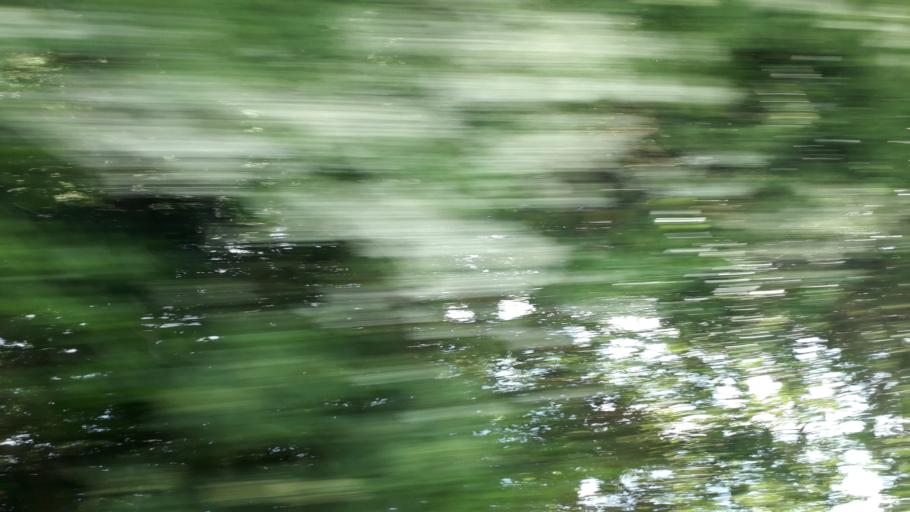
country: IE
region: Leinster
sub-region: Kildare
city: Moone
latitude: 53.0106
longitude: -6.8062
